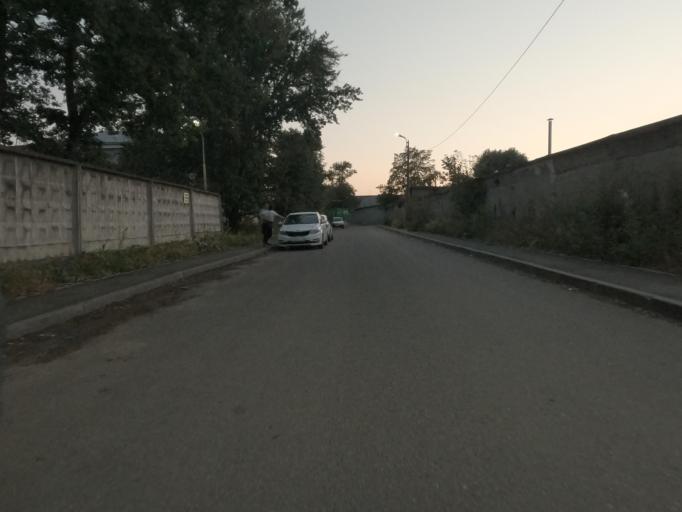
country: RU
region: St.-Petersburg
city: Avtovo
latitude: 59.8728
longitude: 30.2873
